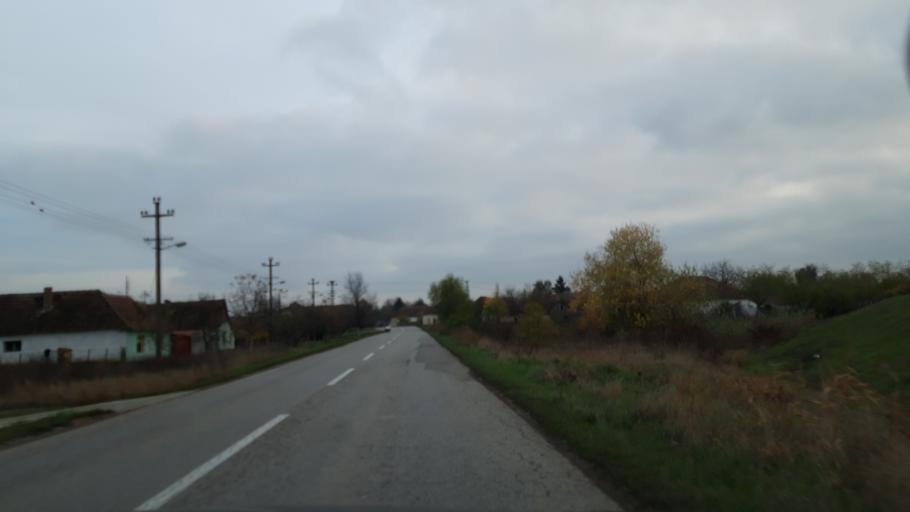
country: RS
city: Sanad
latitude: 45.9827
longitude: 20.1119
